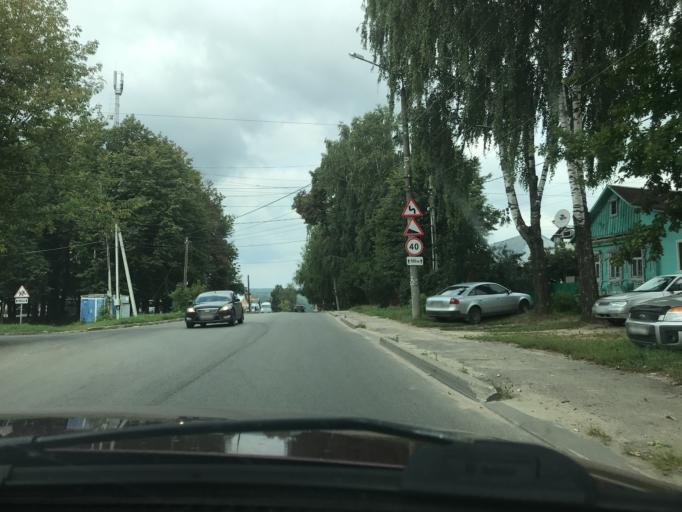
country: RU
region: Kaluga
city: Kaluga
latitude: 54.5354
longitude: 36.2492
